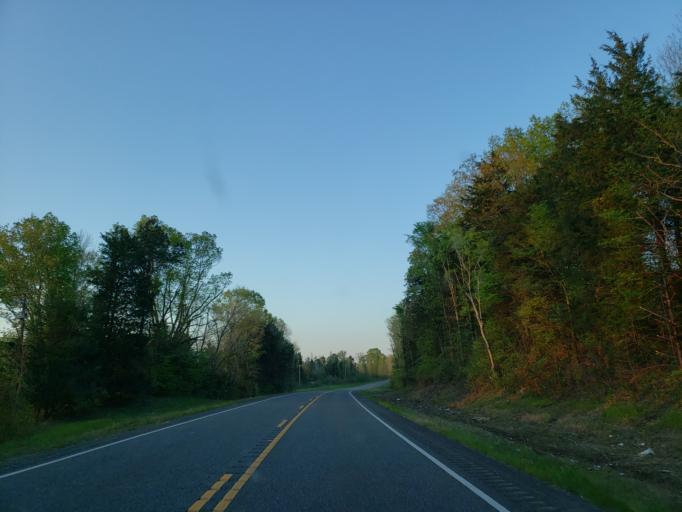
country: US
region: Alabama
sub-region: Sumter County
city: Livingston
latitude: 32.6488
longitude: -88.1709
